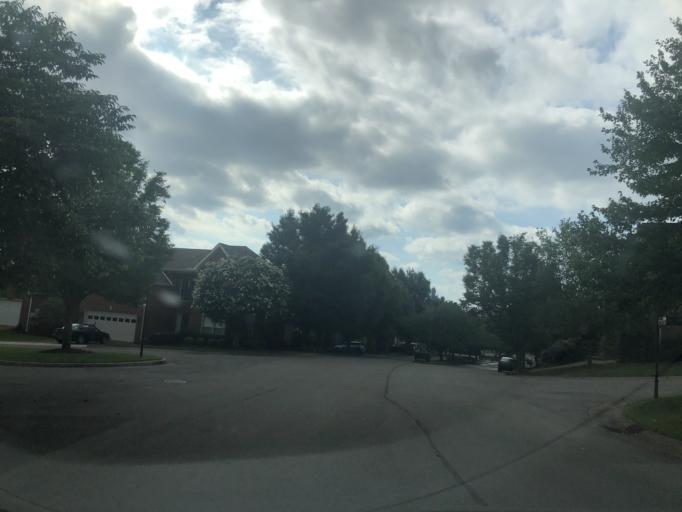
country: US
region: Tennessee
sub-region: Davidson County
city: Oak Hill
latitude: 36.0919
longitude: -86.8150
